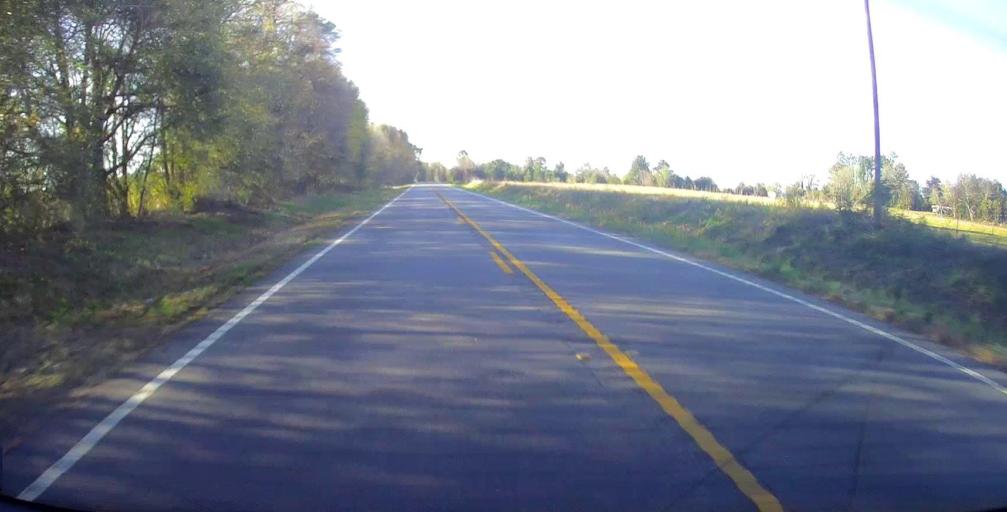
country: US
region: Georgia
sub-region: Pulaski County
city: Hawkinsville
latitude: 32.2302
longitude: -83.3953
